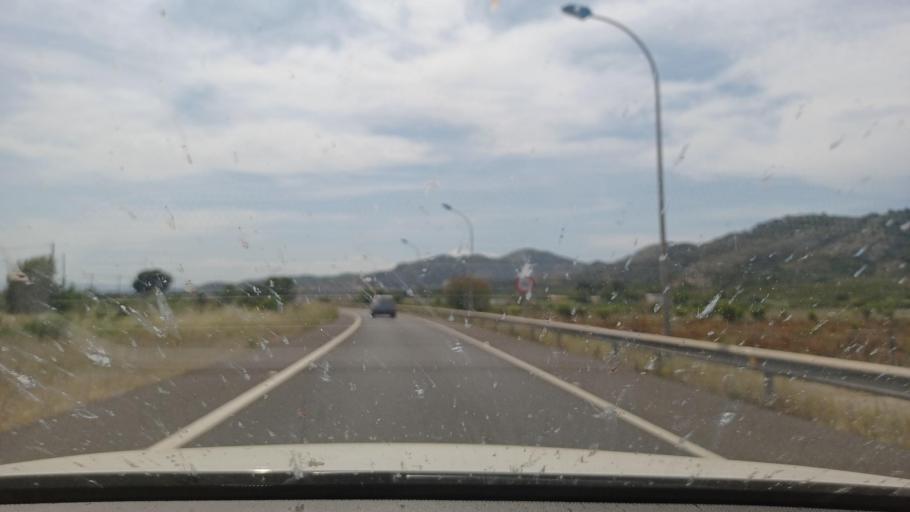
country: ES
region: Valencia
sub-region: Provincia de Castello
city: Castello de la Plana
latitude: 40.0237
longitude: -0.0261
